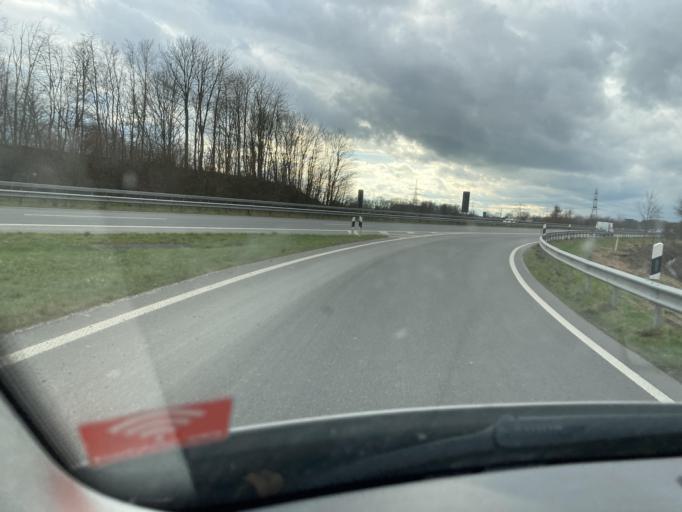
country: DE
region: Lower Saxony
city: Fedderwarden
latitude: 53.5589
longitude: 8.0763
